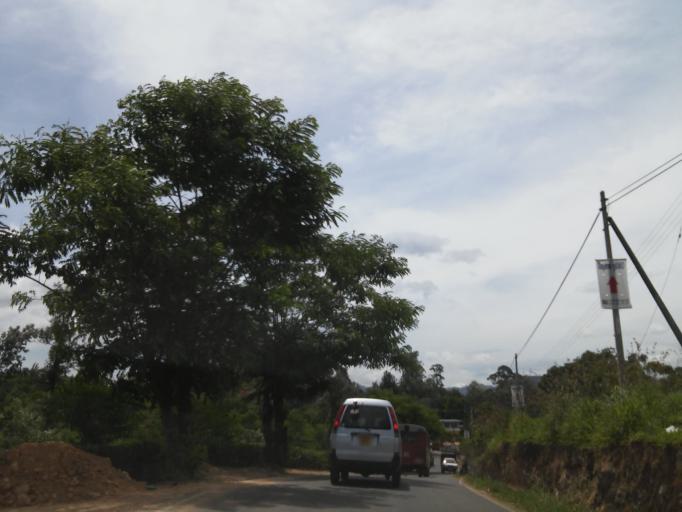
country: LK
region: Uva
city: Haputale
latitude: 6.8416
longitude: 81.0153
